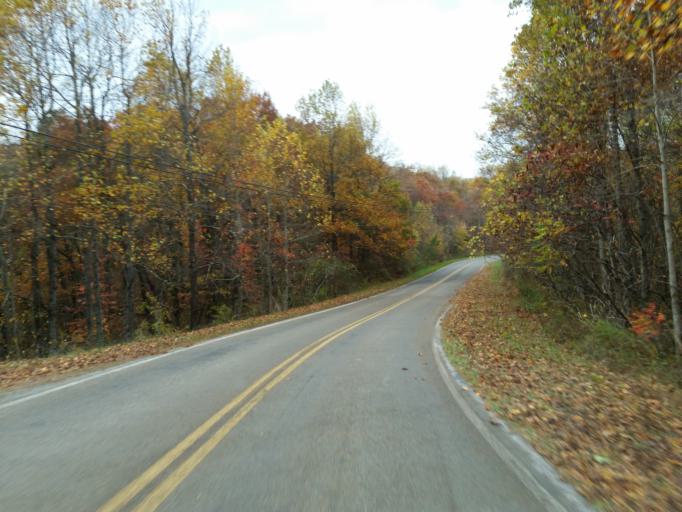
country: US
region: Georgia
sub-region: Pickens County
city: Jasper
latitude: 34.5546
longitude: -84.3530
